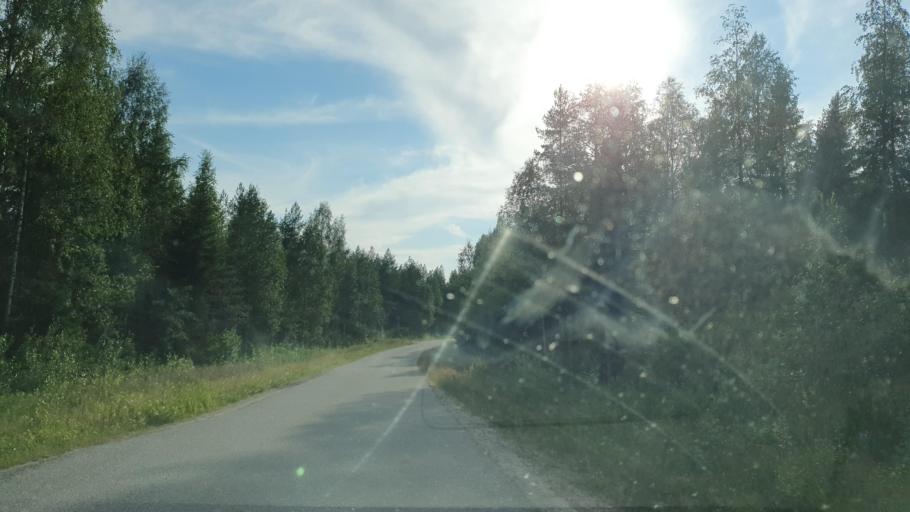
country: FI
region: Kainuu
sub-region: Kehys-Kainuu
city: Kuhmo
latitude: 64.2761
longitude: 29.4426
